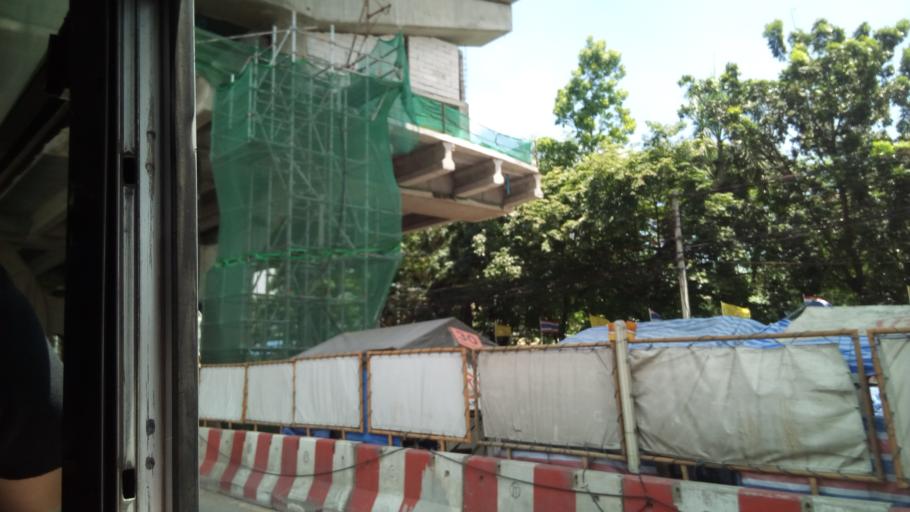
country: TH
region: Bangkok
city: Lak Si
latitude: 13.8567
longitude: 100.5857
